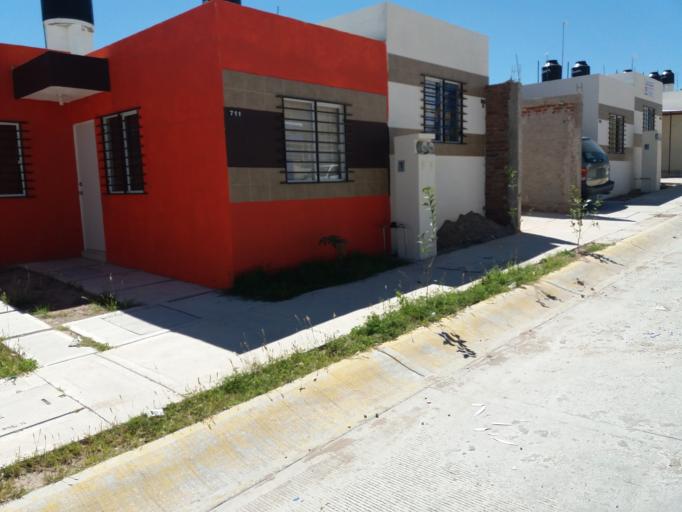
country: MX
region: Aguascalientes
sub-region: Aguascalientes
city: Cumbres III
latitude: 21.8720
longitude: -102.2278
